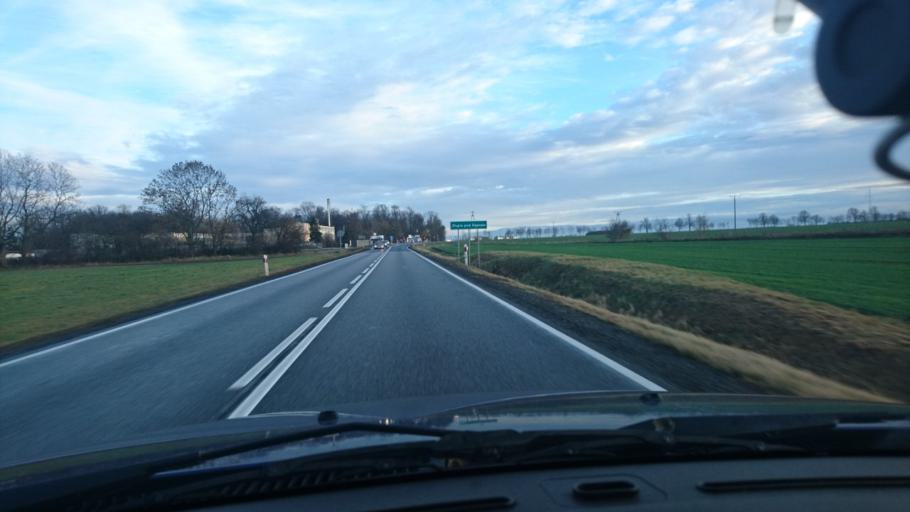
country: PL
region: Greater Poland Voivodeship
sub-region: Powiat kepinski
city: Slupia pod Kepnem
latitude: 51.2425
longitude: 18.0296
